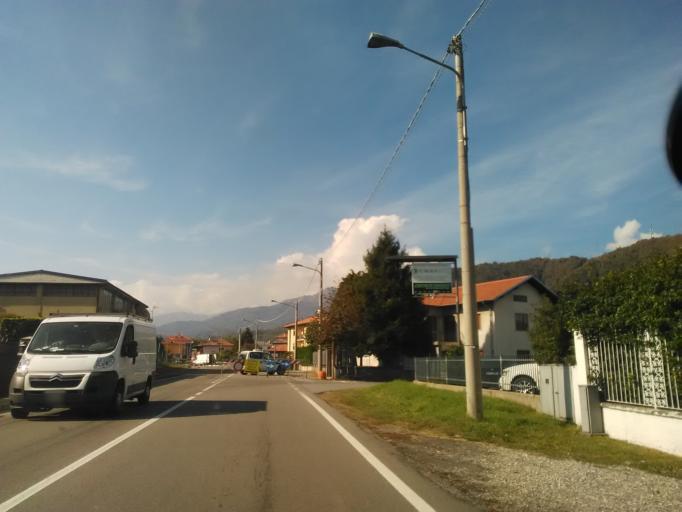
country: IT
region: Piedmont
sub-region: Provincia di Vercelli
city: Serravalle Sesia
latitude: 45.6971
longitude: 8.2900
